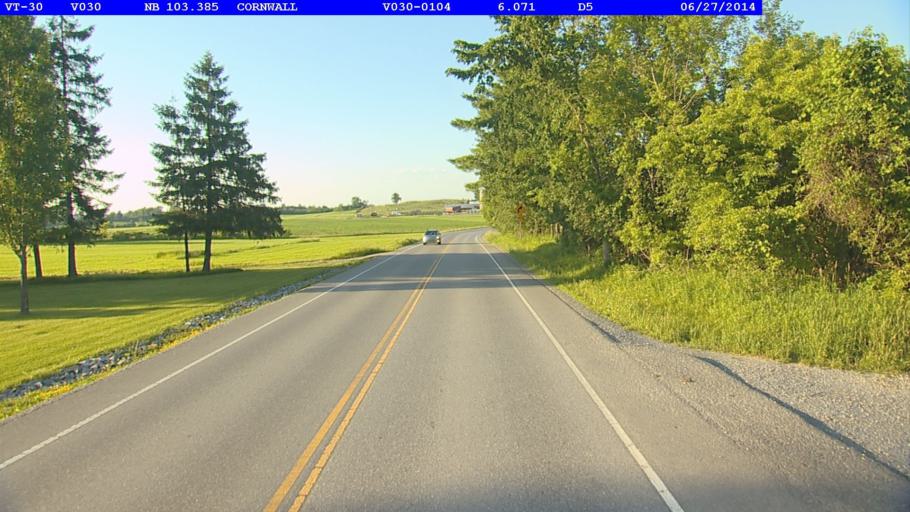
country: US
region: Vermont
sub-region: Addison County
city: Middlebury (village)
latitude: 43.9920
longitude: -73.1938
